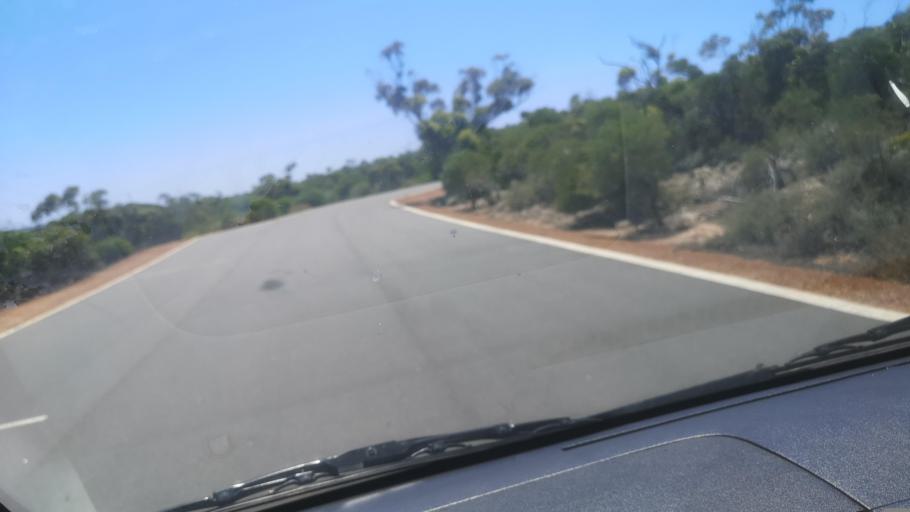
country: AU
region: Western Australia
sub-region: Northampton Shire
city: Kalbarri
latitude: -27.6972
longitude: 114.2173
